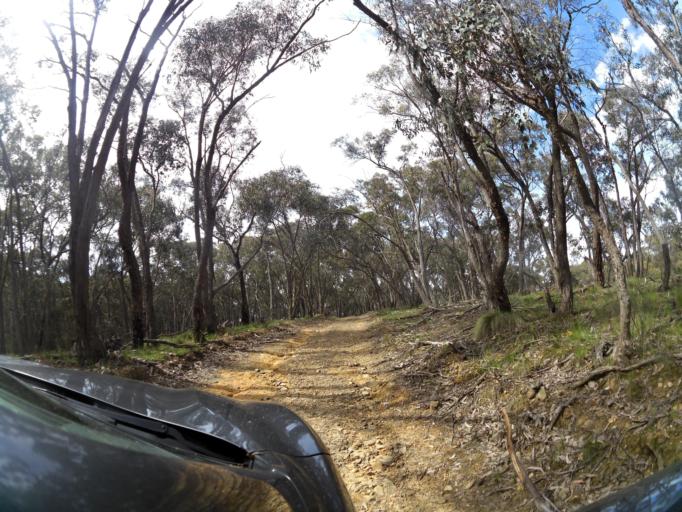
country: AU
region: Victoria
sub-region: Mount Alexander
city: Castlemaine
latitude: -37.3062
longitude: 144.1447
